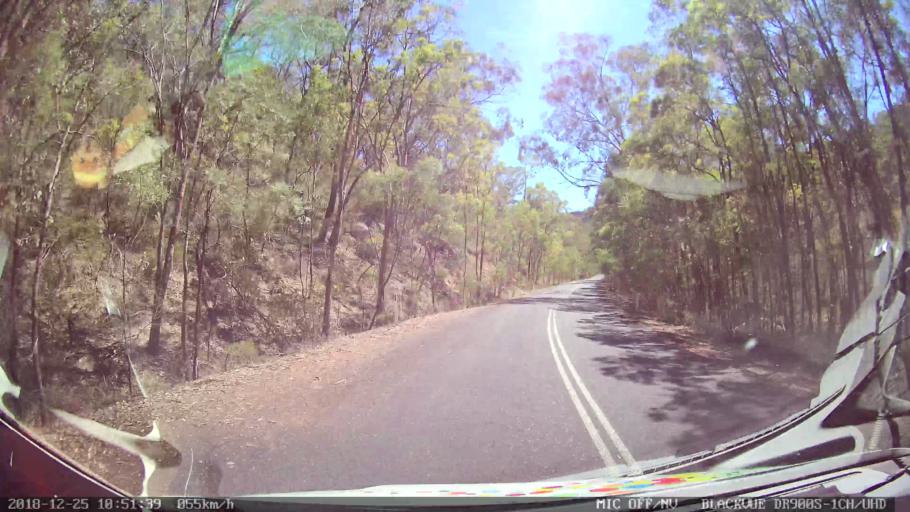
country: AU
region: New South Wales
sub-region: Upper Hunter Shire
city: Merriwa
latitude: -32.4349
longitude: 150.2696
